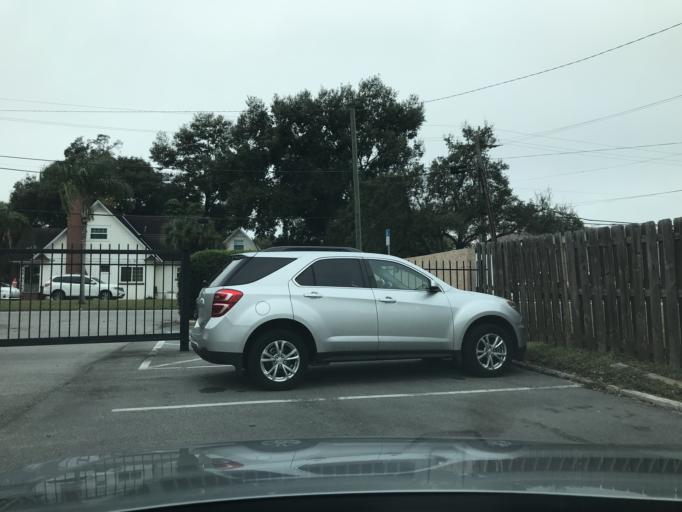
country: US
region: Florida
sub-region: Hillsborough County
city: Egypt Lake-Leto
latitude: 27.9953
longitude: -82.4677
